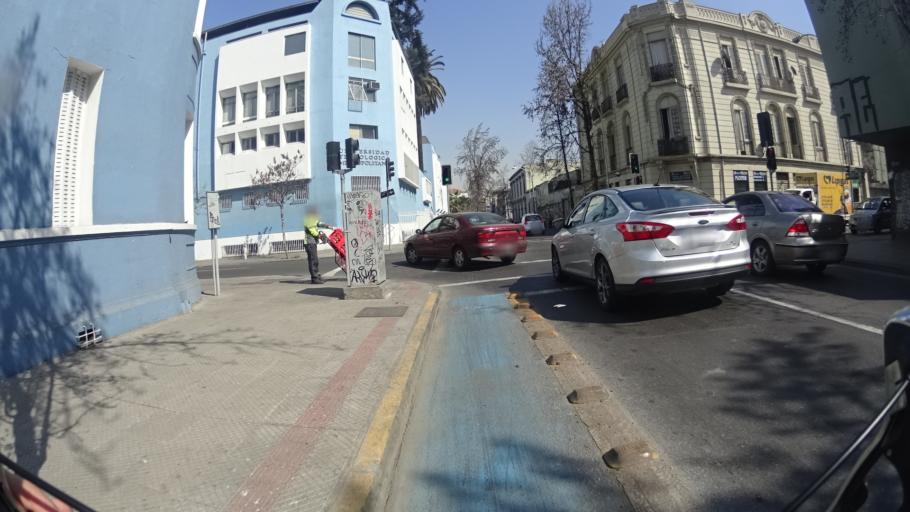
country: CL
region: Santiago Metropolitan
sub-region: Provincia de Santiago
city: Santiago
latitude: -33.4481
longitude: -70.6566
